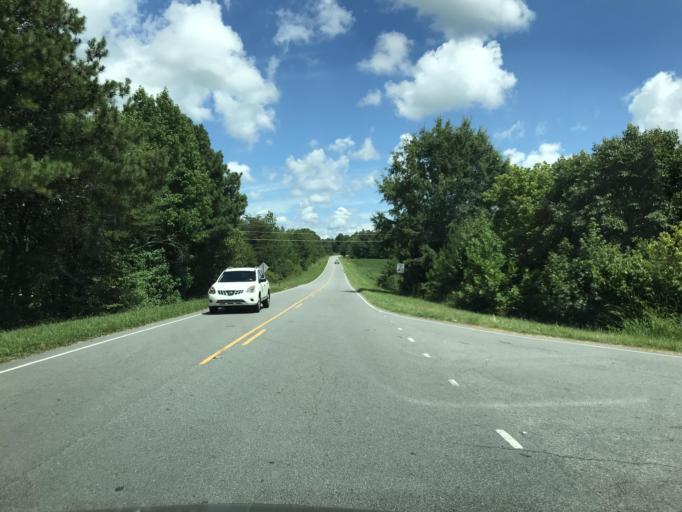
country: US
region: North Carolina
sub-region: Lincoln County
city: Lincolnton
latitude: 35.5051
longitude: -81.2231
